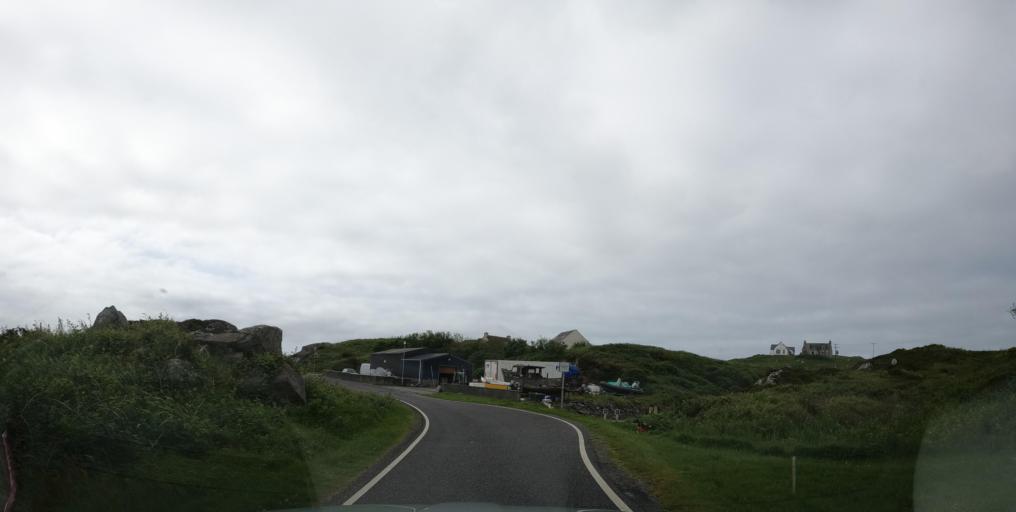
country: GB
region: Scotland
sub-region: Eilean Siar
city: Isle of South Uist
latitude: 57.1048
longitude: -7.3269
